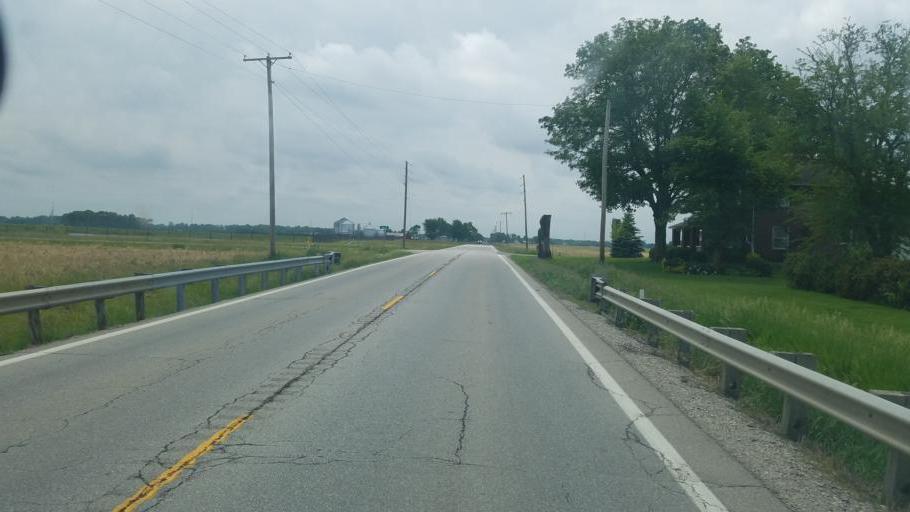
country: US
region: Ohio
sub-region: Union County
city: Richwood
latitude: 40.4126
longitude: -83.2546
